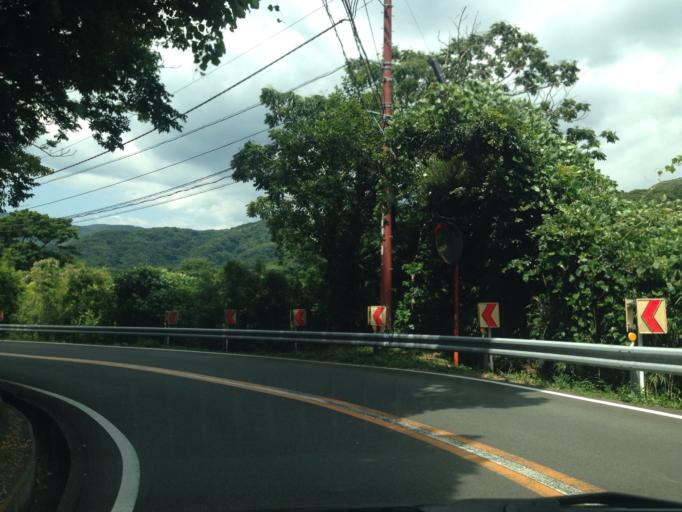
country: JP
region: Shizuoka
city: Shimoda
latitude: 34.6553
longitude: 138.7928
